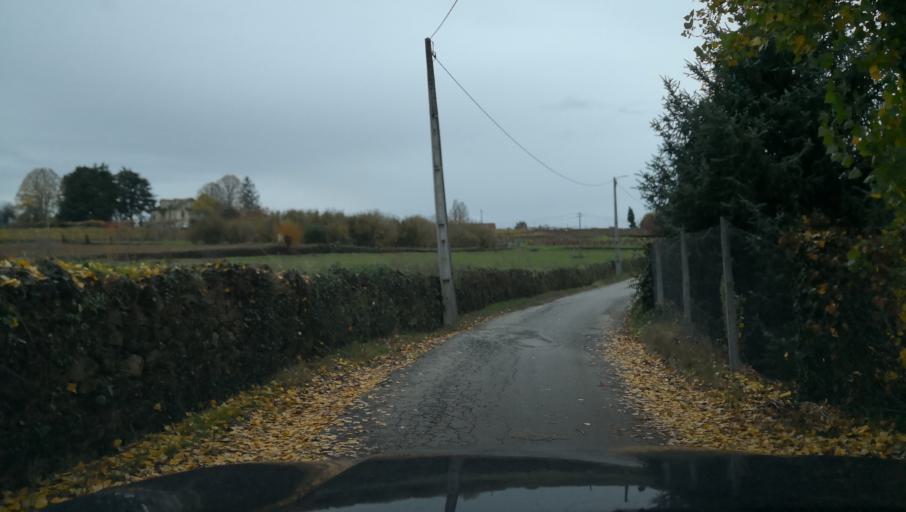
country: PT
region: Vila Real
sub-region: Vila Real
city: Vila Real
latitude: 41.2887
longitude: -7.7363
